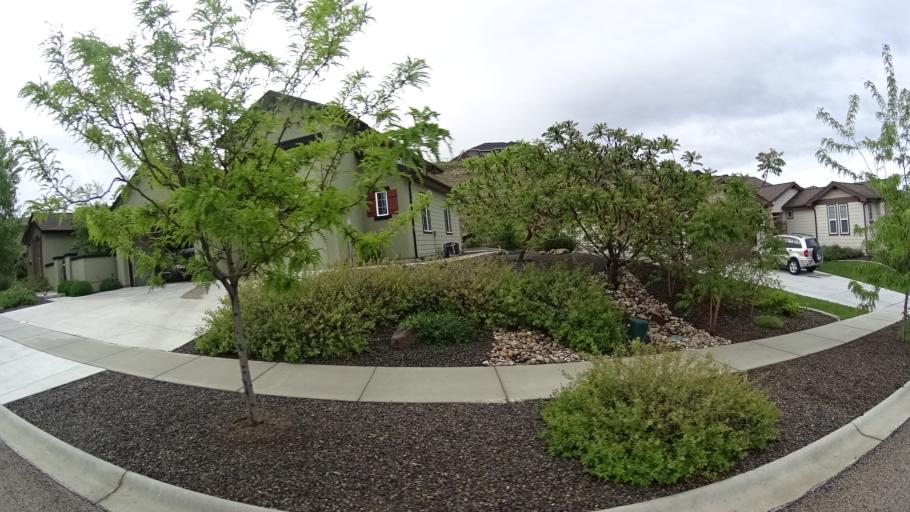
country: US
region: Idaho
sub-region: Ada County
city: Eagle
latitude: 43.7732
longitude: -116.2587
